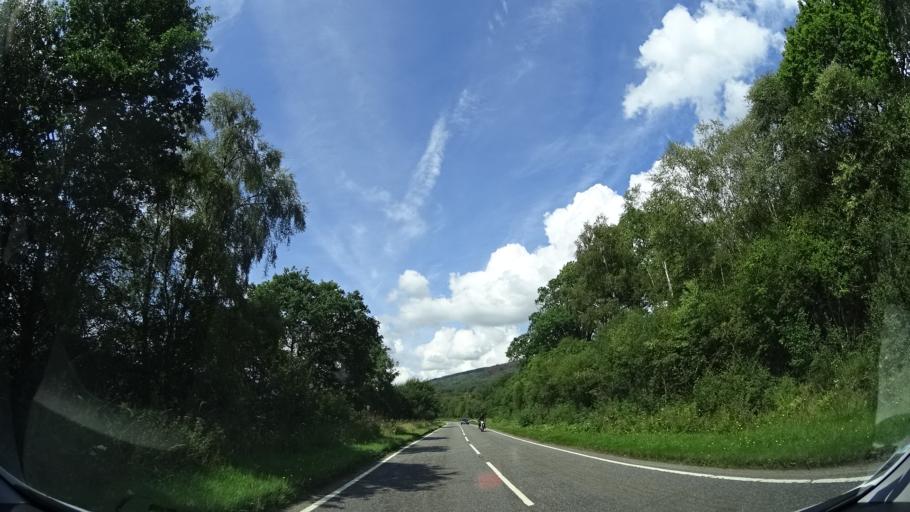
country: GB
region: Scotland
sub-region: Highland
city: Fort William
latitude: 56.8512
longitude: -5.1711
